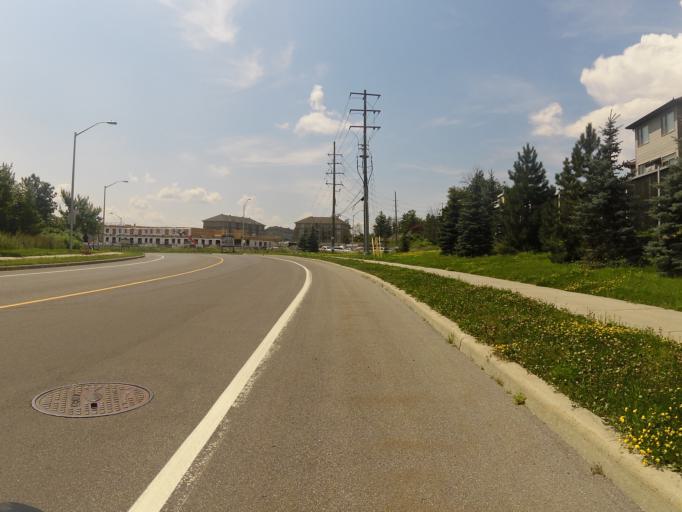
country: CA
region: Ontario
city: Bells Corners
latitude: 45.3177
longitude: -75.9315
